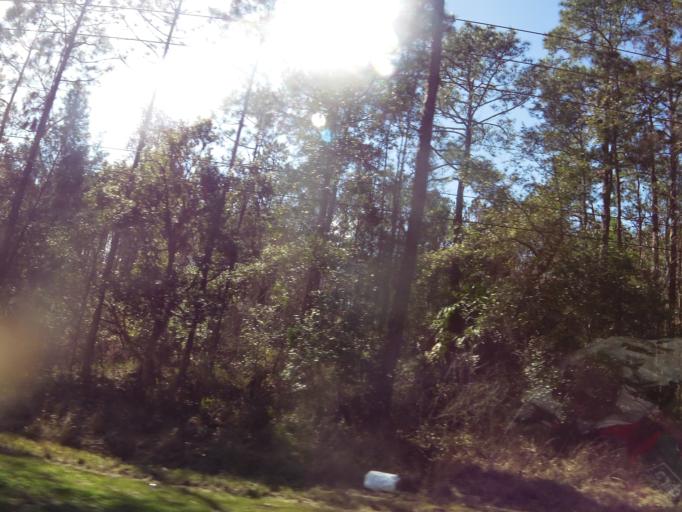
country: US
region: Florida
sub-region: Volusia County
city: Pierson
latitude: 29.1931
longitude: -81.4284
